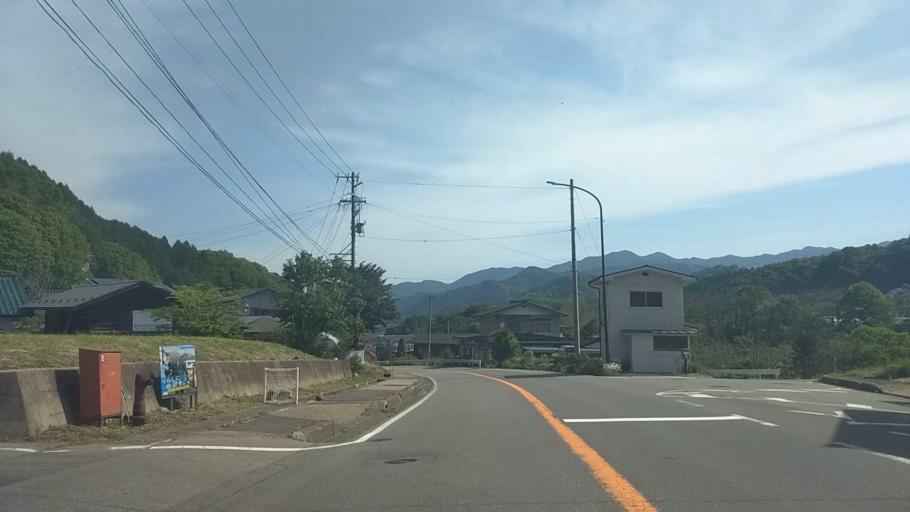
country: JP
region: Nagano
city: Saku
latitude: 36.0766
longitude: 138.4783
